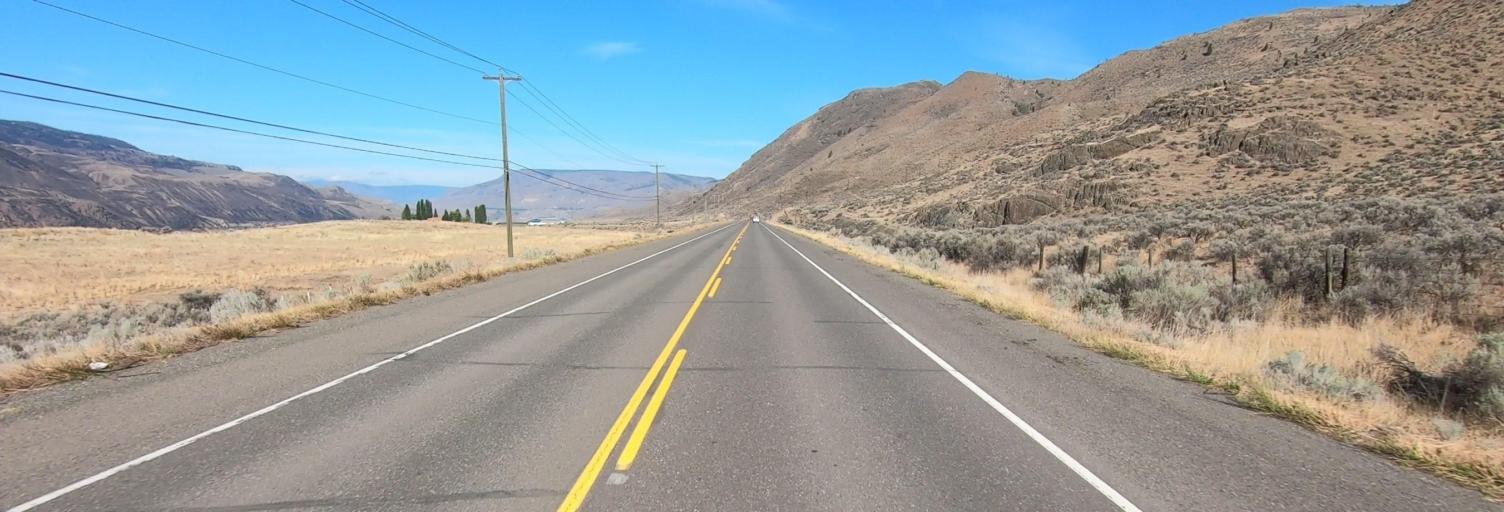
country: CA
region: British Columbia
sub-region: Thompson-Nicola Regional District
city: Ashcroft
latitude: 50.7653
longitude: -121.0018
